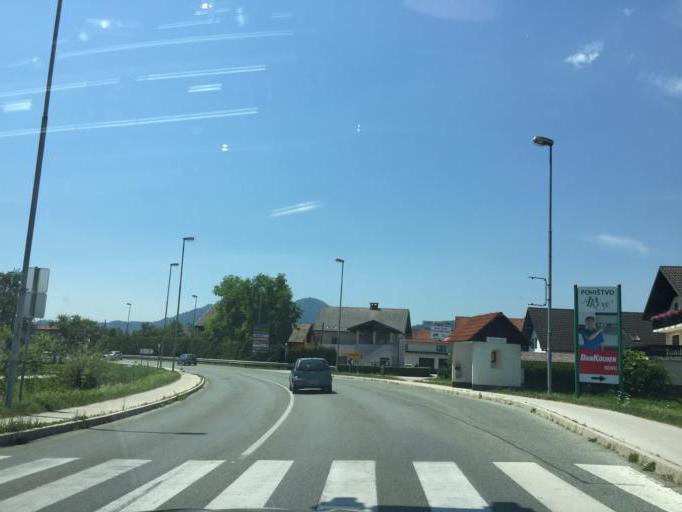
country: SI
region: Skofja Loka
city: Sv. Duh
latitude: 46.1951
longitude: 14.3256
